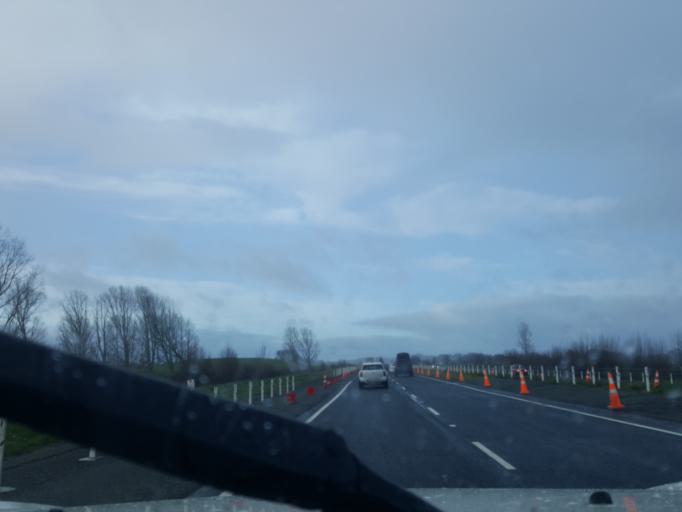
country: NZ
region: Waikato
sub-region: Waikato District
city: Ngaruawahia
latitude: -37.6463
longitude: 175.2063
